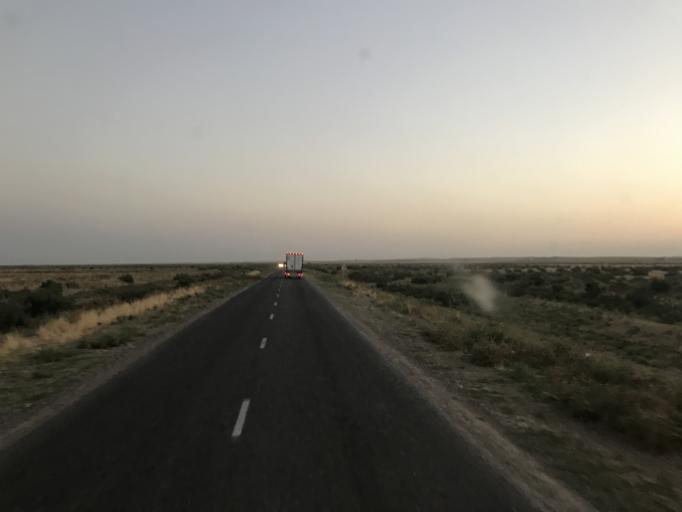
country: UZ
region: Toshkent
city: Chinoz
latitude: 41.2141
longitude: 68.5987
